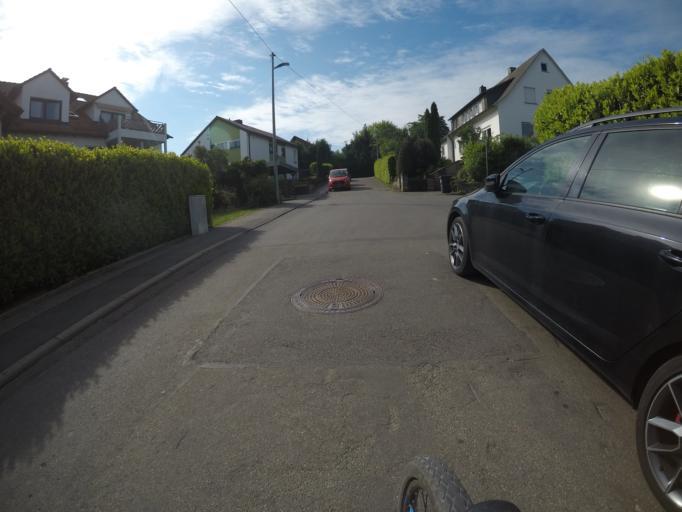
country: DE
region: Baden-Wuerttemberg
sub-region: Regierungsbezirk Stuttgart
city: Neuhausen auf den Fildern
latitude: 48.6767
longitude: 9.2795
